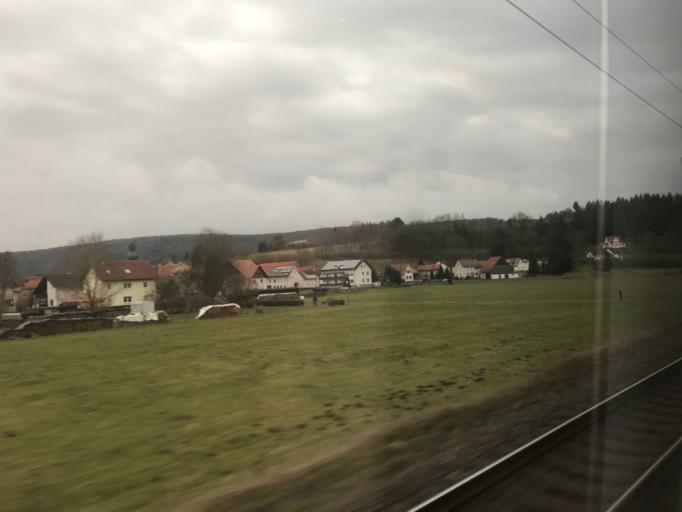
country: DE
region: Hesse
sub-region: Regierungsbezirk Kassel
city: Burghaun
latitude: 50.7230
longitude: 9.7077
